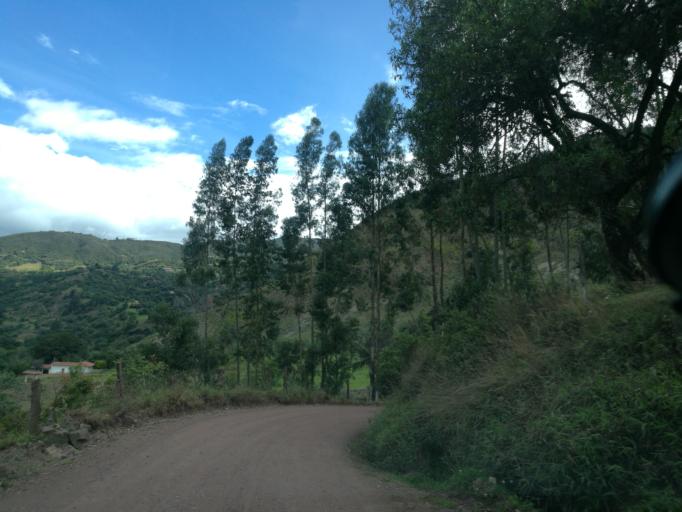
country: CO
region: Boyaca
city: Susacon
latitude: 6.1207
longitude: -72.7134
